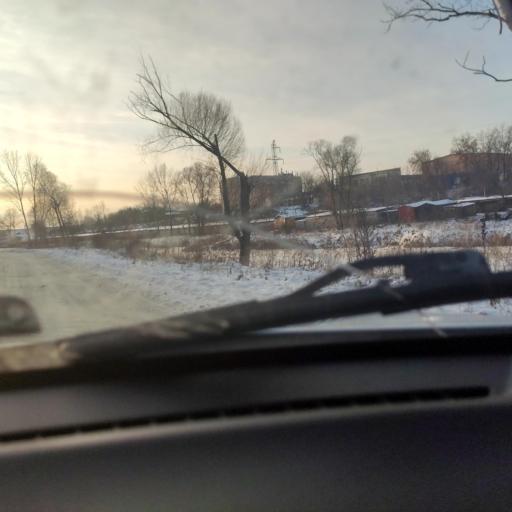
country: RU
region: Tatarstan
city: Verkhniy Uslon
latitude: 55.8010
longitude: 49.0475
